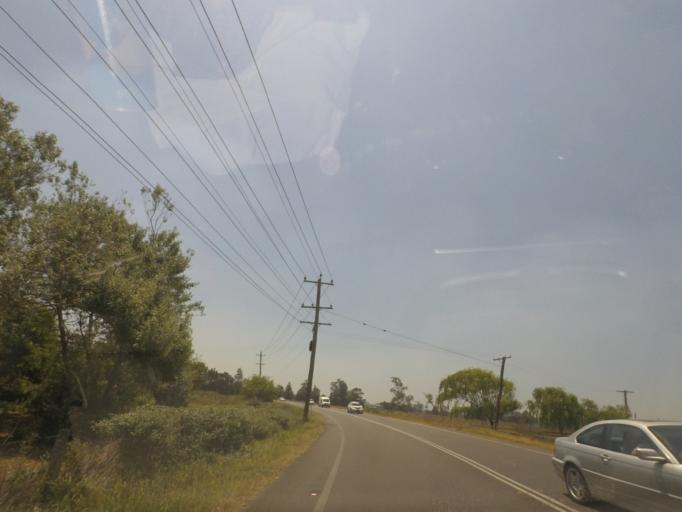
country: AU
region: New South Wales
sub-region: Port Stephens Shire
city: Medowie
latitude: -32.8019
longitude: 151.8877
